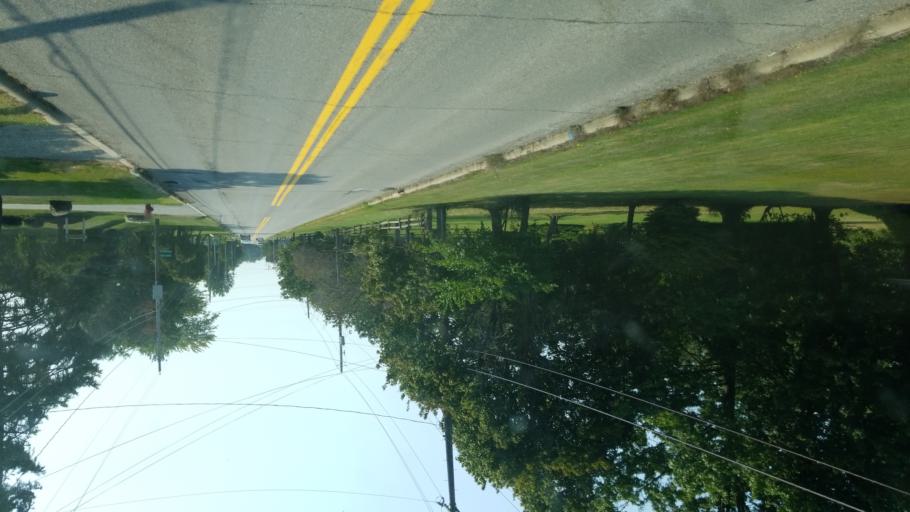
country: US
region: Ohio
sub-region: Lake County
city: Painesville
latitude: 41.7266
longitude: -81.2038
